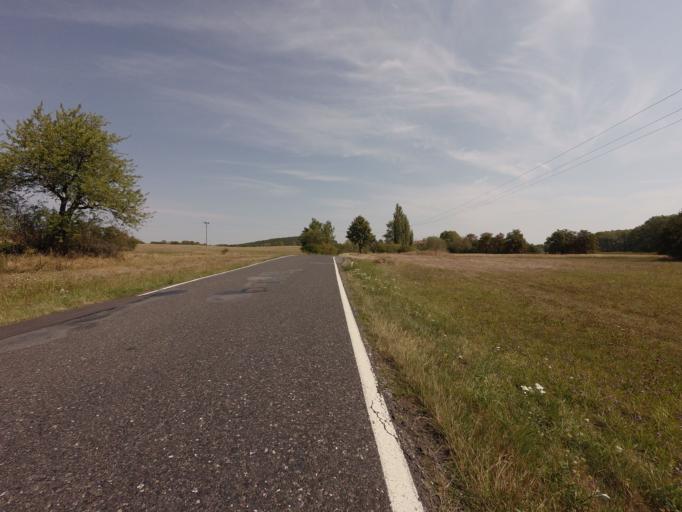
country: CZ
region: Central Bohemia
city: Petrovice
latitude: 49.5721
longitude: 14.3709
